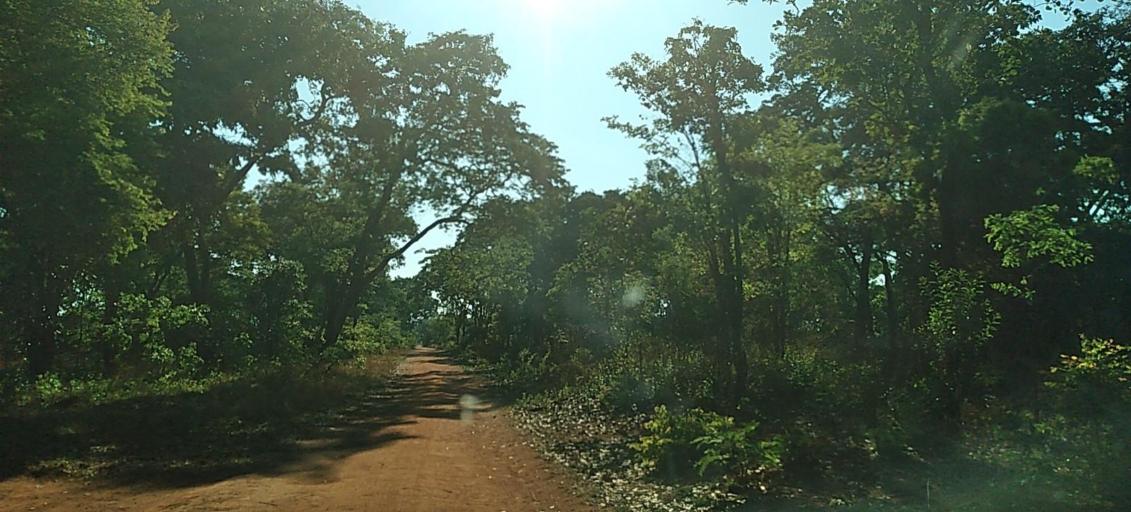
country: ZM
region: Copperbelt
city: Luanshya
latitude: -13.4589
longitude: 28.8299
